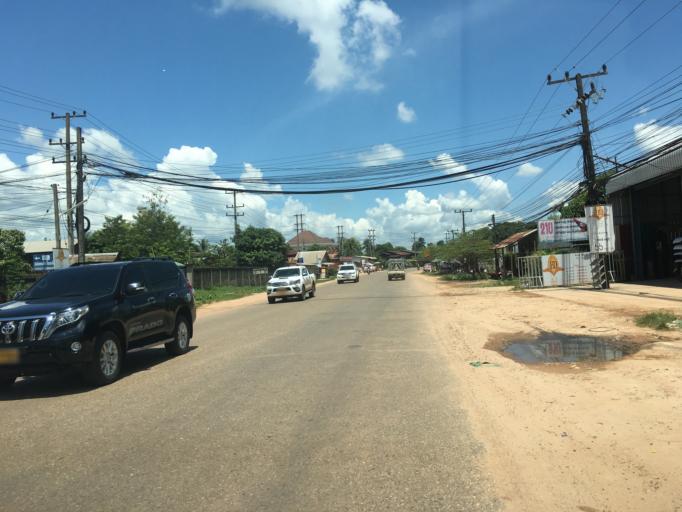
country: LA
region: Vientiane
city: Vientiane
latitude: 18.0671
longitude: 102.5360
